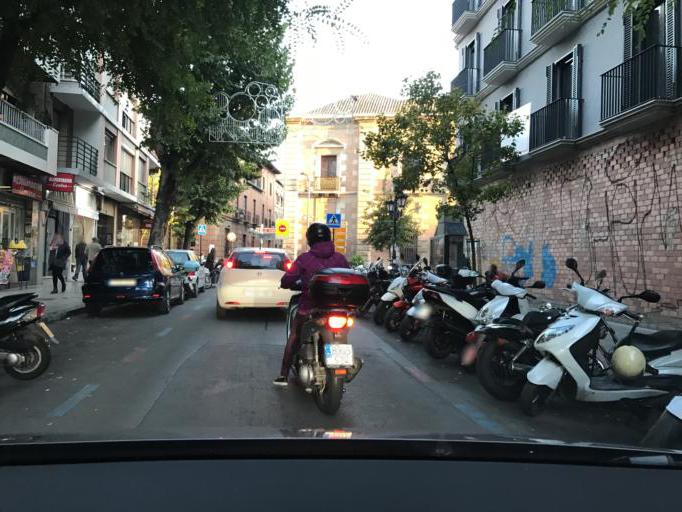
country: ES
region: Andalusia
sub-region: Provincia de Granada
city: Granada
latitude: 37.1760
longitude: -3.6043
